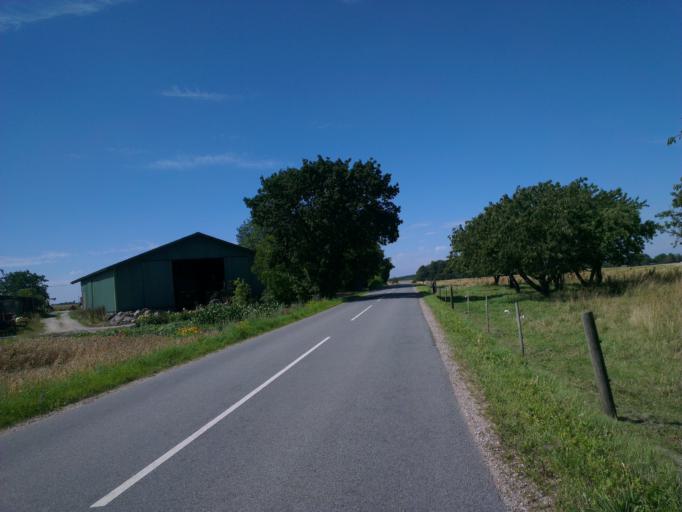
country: DK
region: Capital Region
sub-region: Frederikssund Kommune
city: Slangerup
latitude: 55.8591
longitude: 12.1533
